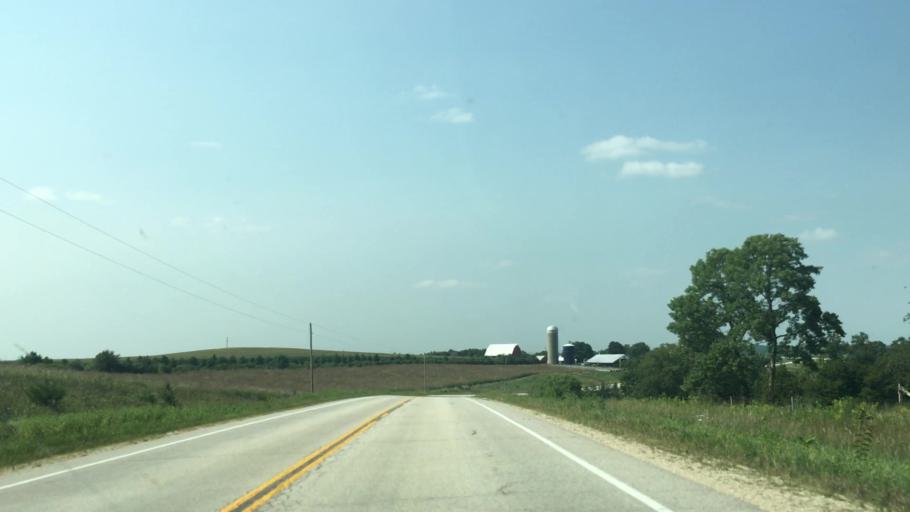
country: US
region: Minnesota
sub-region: Fillmore County
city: Harmony
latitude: 43.6788
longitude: -91.9407
